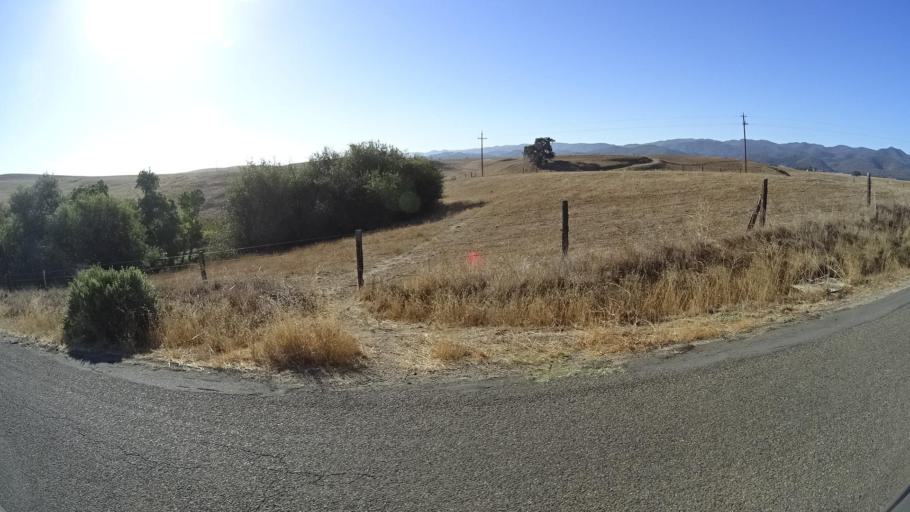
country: US
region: California
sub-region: Monterey County
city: King City
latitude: 36.1119
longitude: -121.0706
